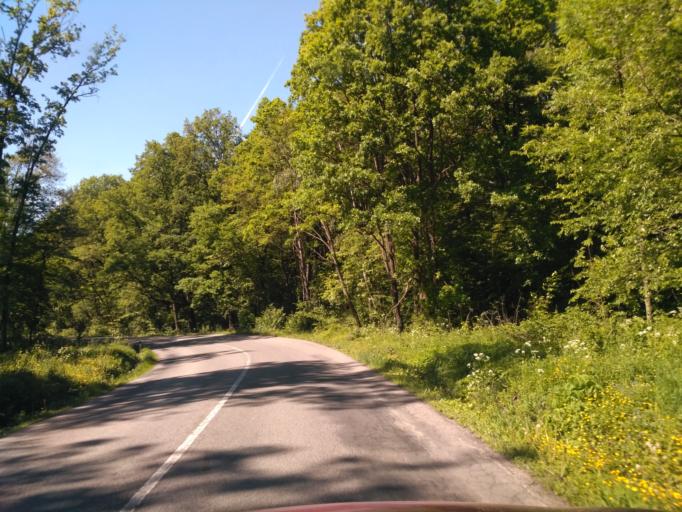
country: SK
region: Presovsky
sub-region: Okres Presov
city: Presov
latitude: 48.9349
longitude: 21.3161
